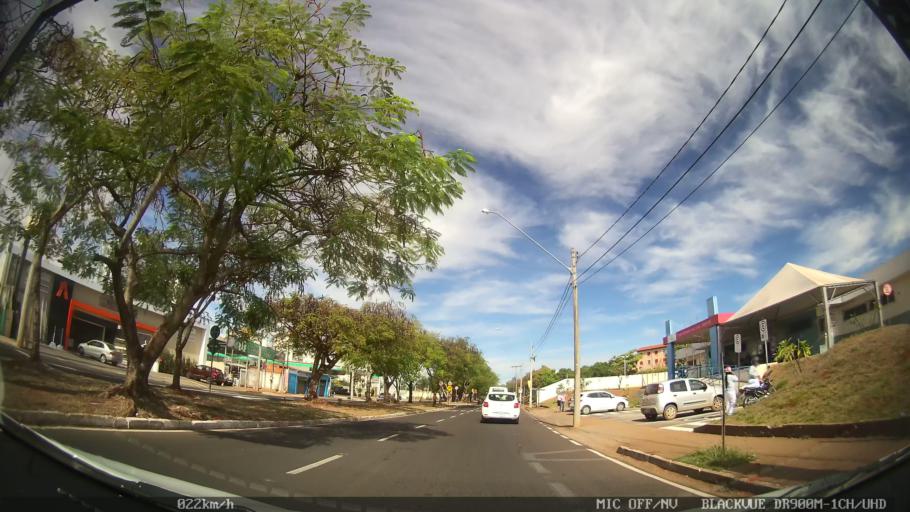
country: BR
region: Sao Paulo
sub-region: Sao Jose Do Rio Preto
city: Sao Jose do Rio Preto
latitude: -20.8252
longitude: -49.3517
